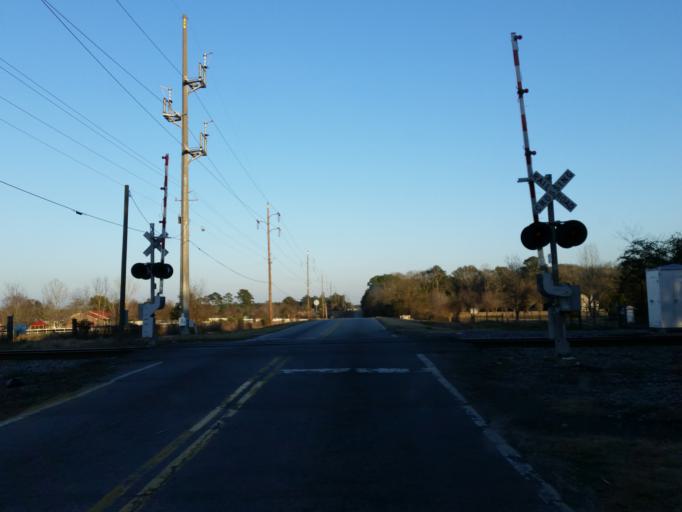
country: US
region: Georgia
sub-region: Crisp County
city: Cordele
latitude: 32.0043
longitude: -83.7858
